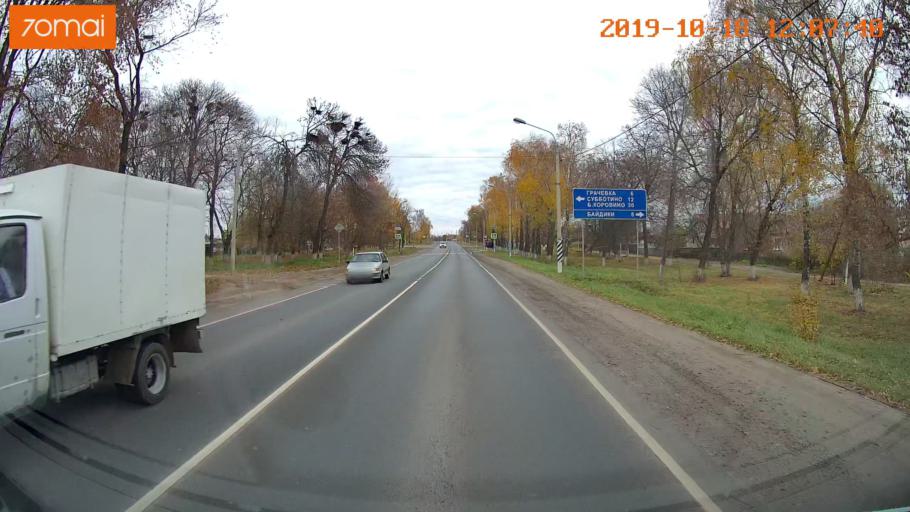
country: RU
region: Rjazan
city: Zakharovo
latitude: 54.3706
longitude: 39.2833
